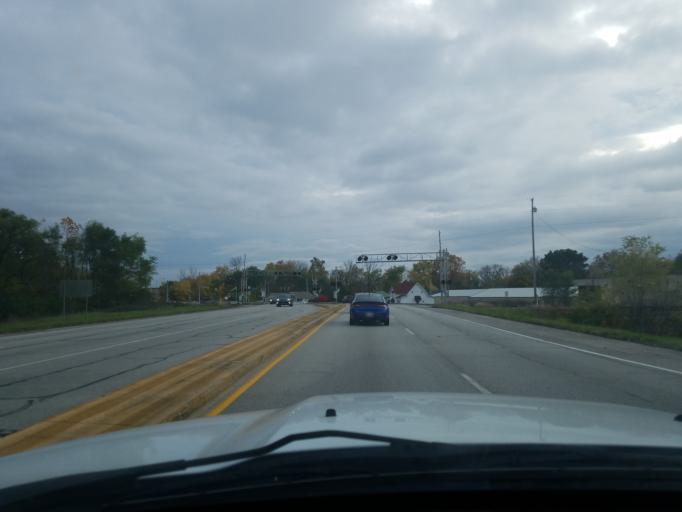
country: US
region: Indiana
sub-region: Shelby County
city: Shelbyville
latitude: 39.5313
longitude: -85.7775
